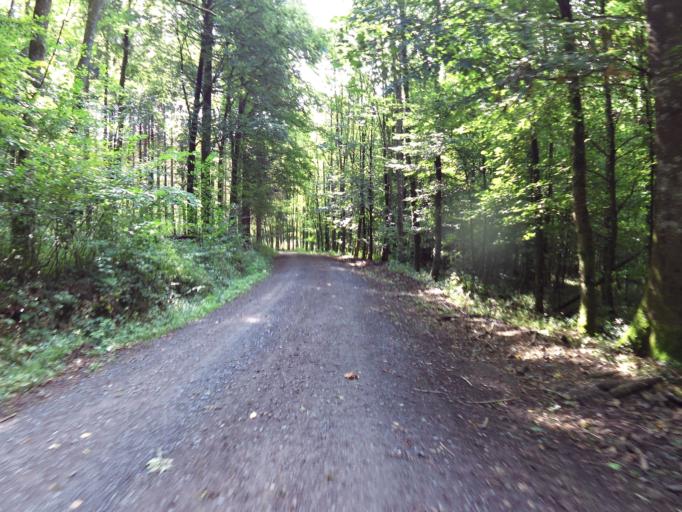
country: DE
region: Baden-Wuerttemberg
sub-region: Karlsruhe Region
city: Wiesenbach
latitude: 49.3482
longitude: 8.8280
